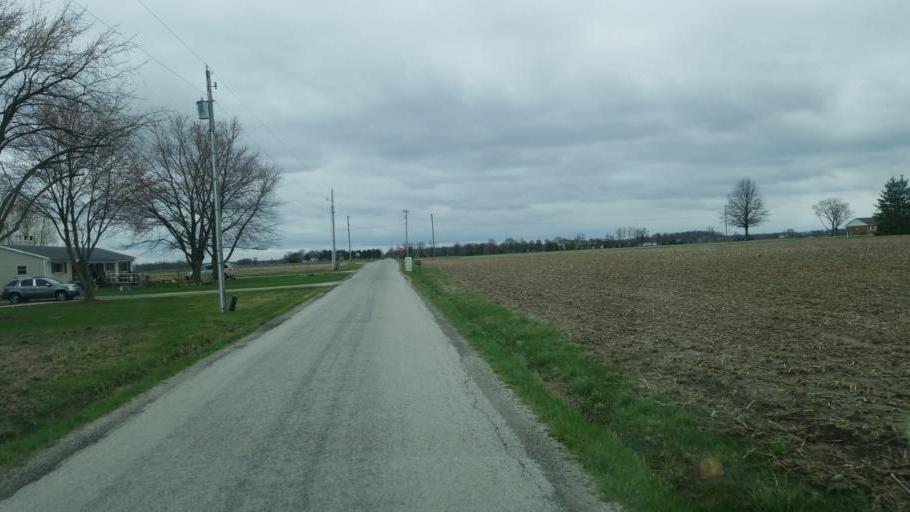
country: US
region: Ohio
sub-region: Marion County
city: Prospect
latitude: 40.4502
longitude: -83.1126
